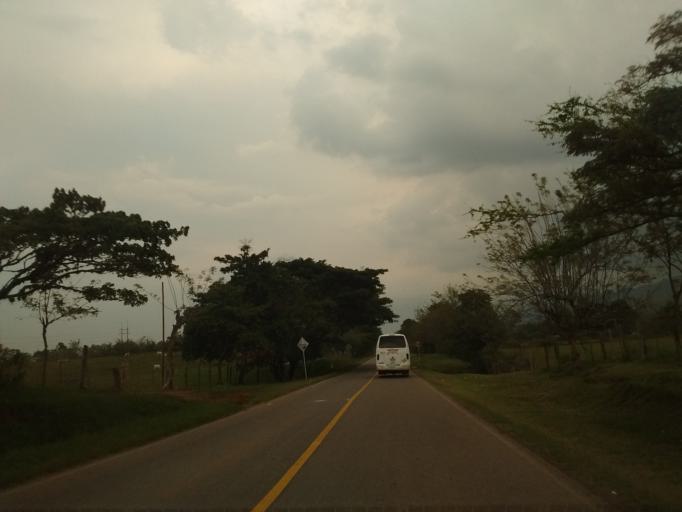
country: CO
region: Cauca
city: Caloto
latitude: 3.0524
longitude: -76.3790
